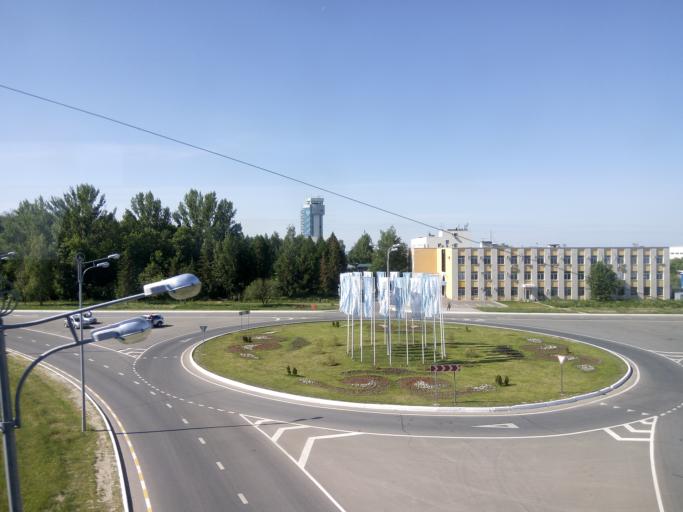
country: RU
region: Tatarstan
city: Stolbishchi
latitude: 55.6146
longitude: 49.2858
